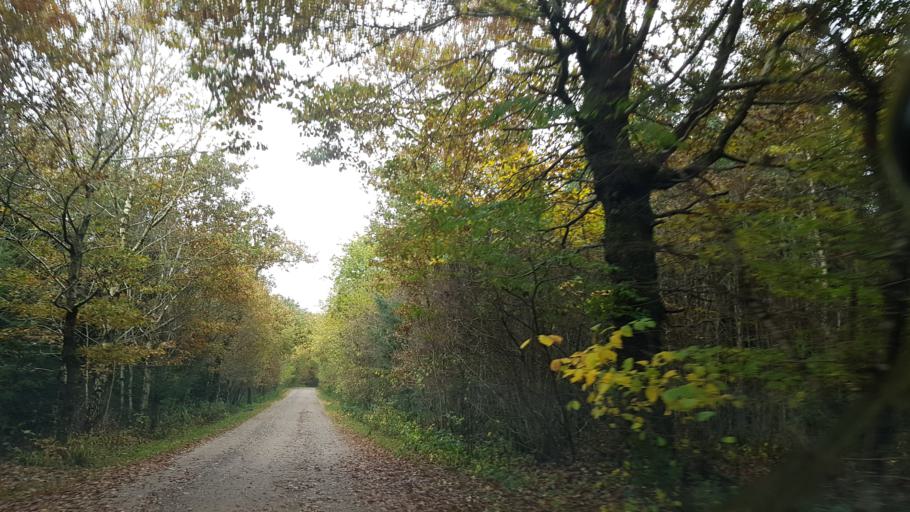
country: DK
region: South Denmark
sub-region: Tonder Kommune
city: Sherrebek
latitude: 55.1755
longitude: 8.7654
